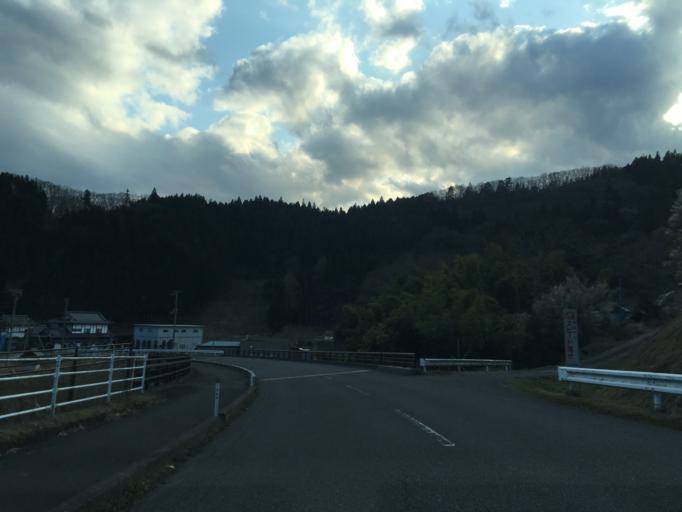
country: JP
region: Fukushima
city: Ishikawa
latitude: 37.1093
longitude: 140.5668
